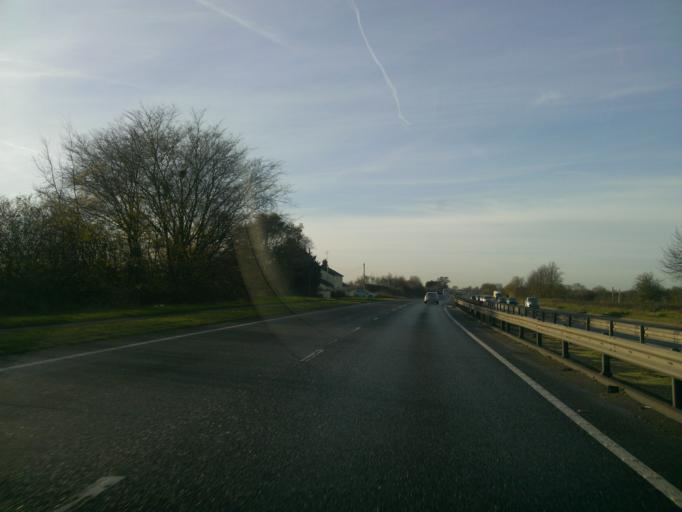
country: GB
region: England
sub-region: Essex
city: Marks Tey
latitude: 51.8706
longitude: 0.7689
